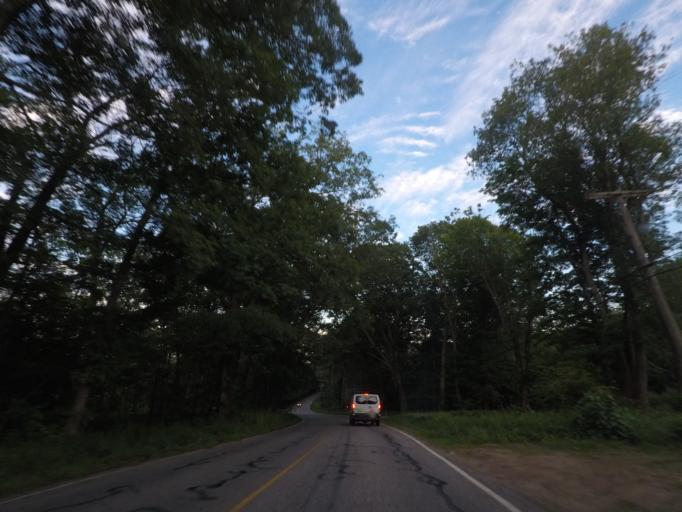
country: US
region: Massachusetts
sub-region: Worcester County
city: Warren
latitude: 42.1692
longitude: -72.1504
